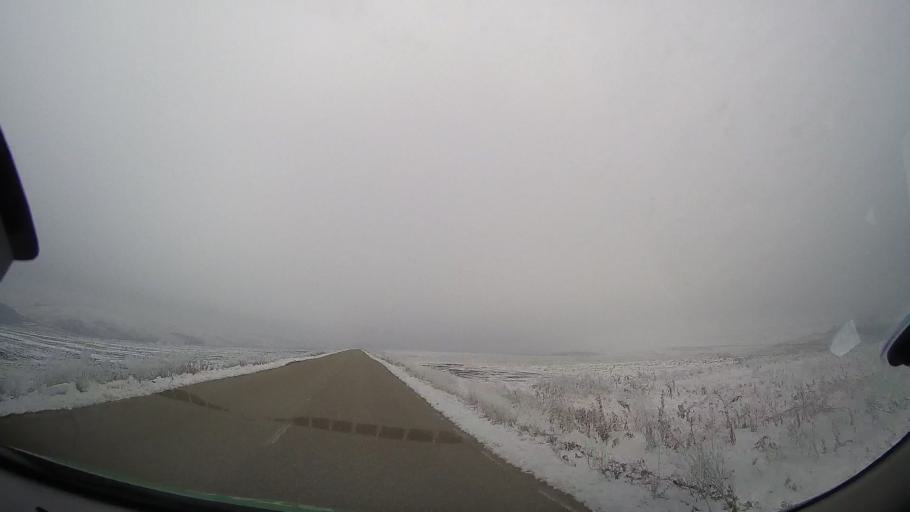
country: RO
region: Vaslui
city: Coroiesti
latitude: 46.2196
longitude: 27.4792
